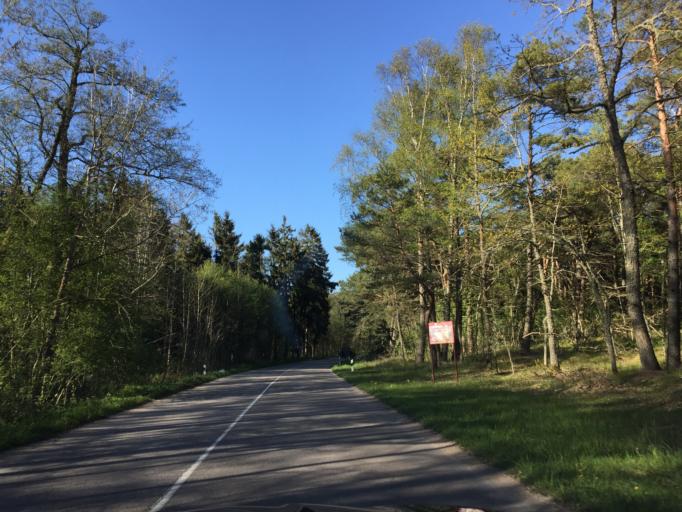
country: LT
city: Nida
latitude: 55.1894
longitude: 20.8584
